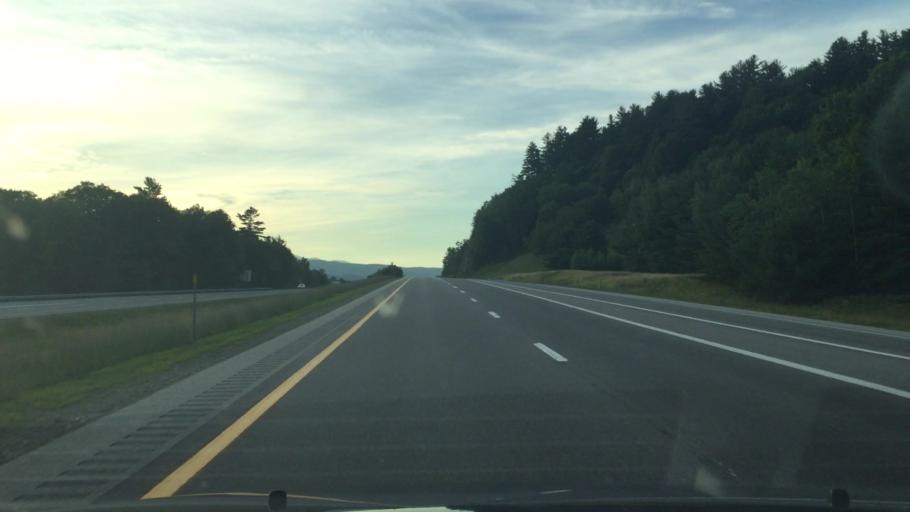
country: US
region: New Hampshire
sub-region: Grafton County
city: Thornton
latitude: 43.8536
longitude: -71.6479
